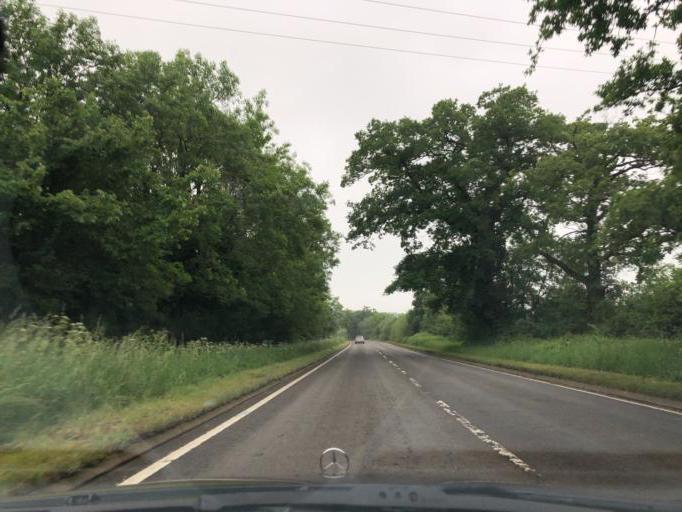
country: GB
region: England
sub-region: Warwickshire
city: Harbury
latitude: 52.2050
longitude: -1.4900
